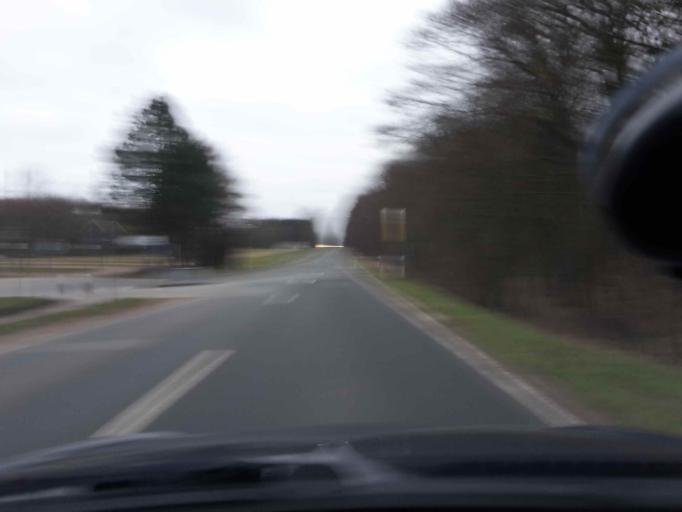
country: DE
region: Lower Saxony
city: Hanstedt
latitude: 53.2357
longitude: 10.0443
